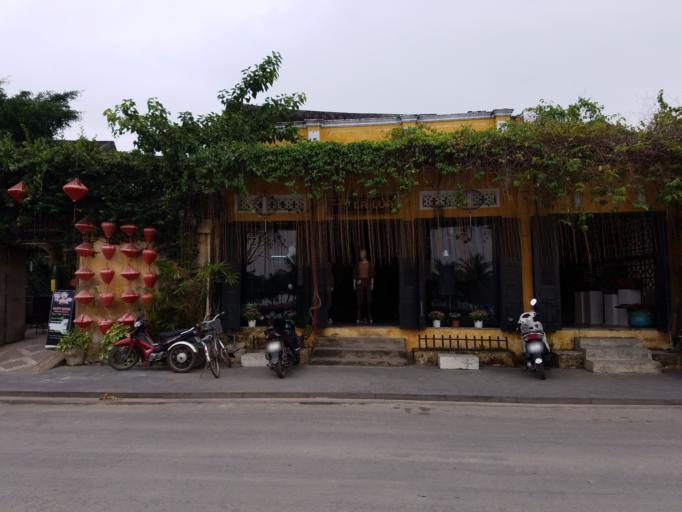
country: VN
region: Quang Nam
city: Hoi An
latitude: 15.8760
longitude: 108.3295
